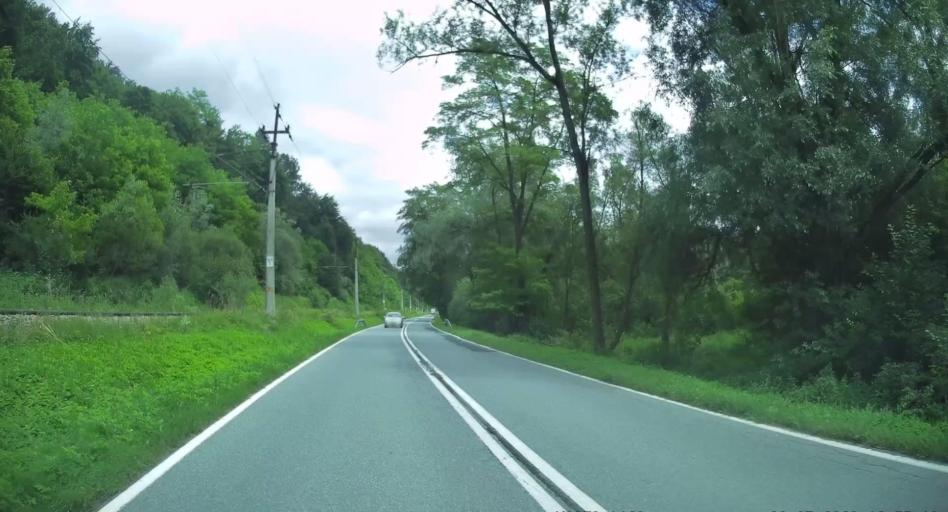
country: PL
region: Lesser Poland Voivodeship
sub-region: Powiat nowosadecki
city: Piwniczna-Zdroj
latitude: 49.3746
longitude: 20.7738
